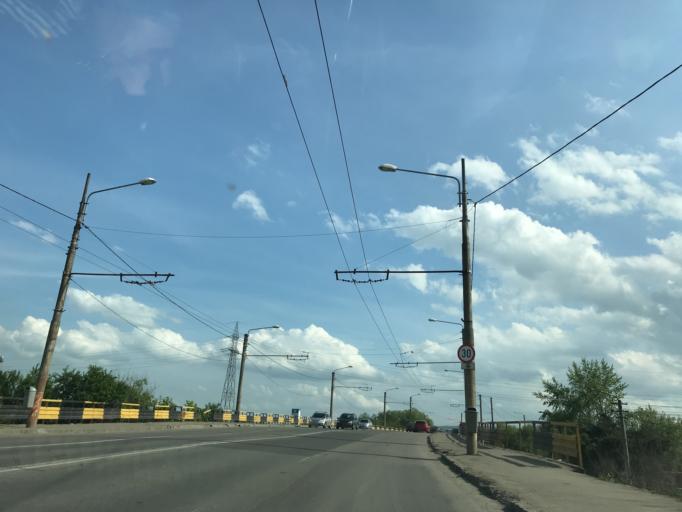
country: RO
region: Cluj
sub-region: Municipiul Cluj-Napoca
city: Cluj-Napoca
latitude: 46.7932
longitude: 23.6152
